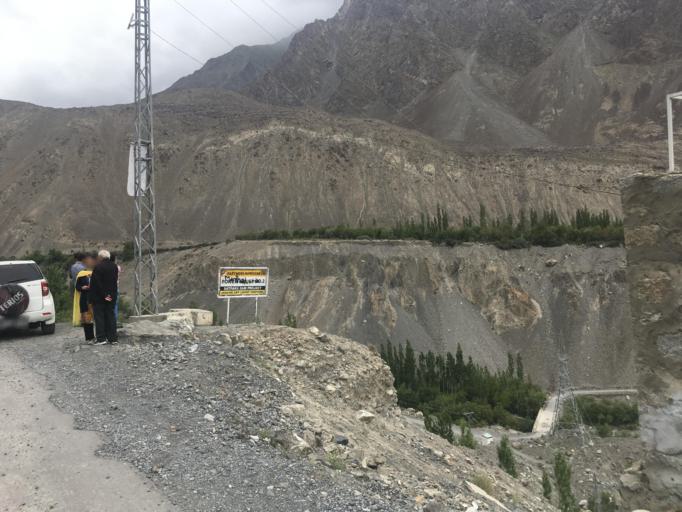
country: PK
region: Gilgit-Baltistan
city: Skardu
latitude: 35.2628
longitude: 75.6374
